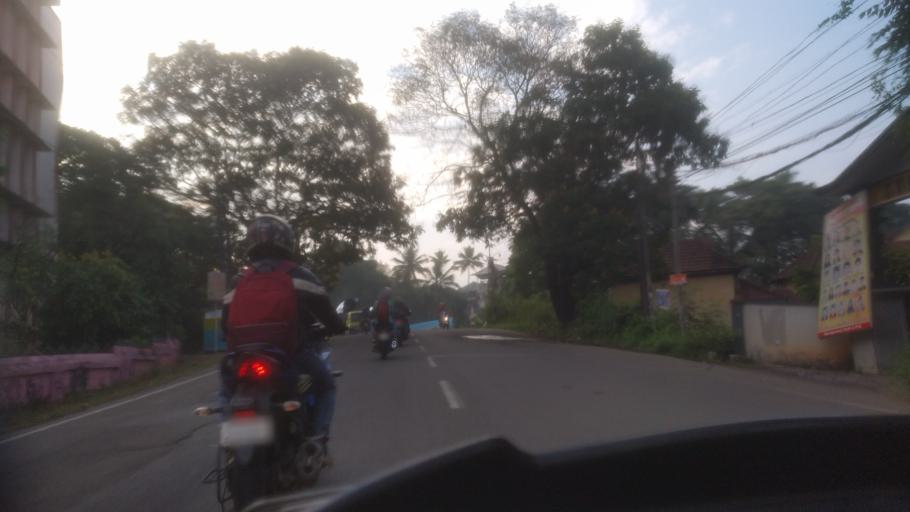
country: IN
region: Kerala
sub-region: Ernakulam
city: Aluva
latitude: 10.1115
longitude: 76.3584
